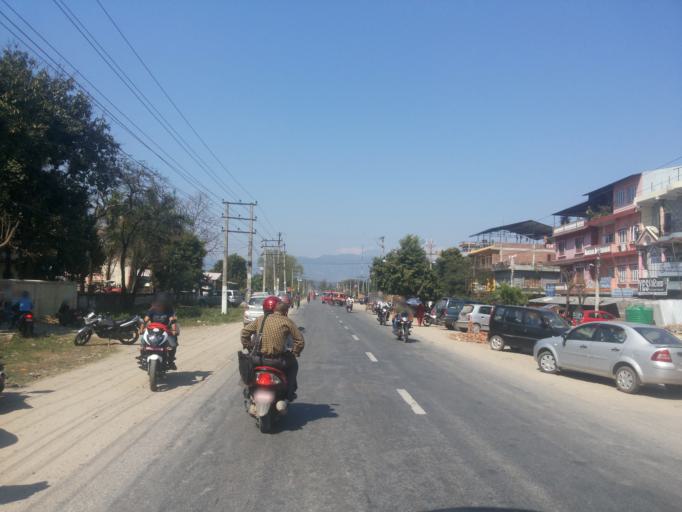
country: NP
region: Central Region
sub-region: Narayani Zone
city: Bharatpur
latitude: 27.6806
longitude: 84.4394
